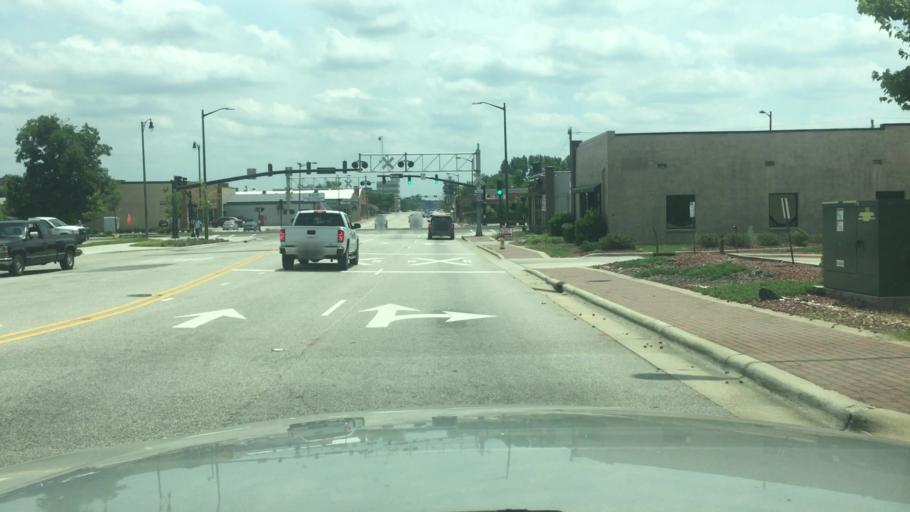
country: US
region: North Carolina
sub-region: Cumberland County
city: Fayetteville
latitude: 35.0532
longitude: -78.8871
